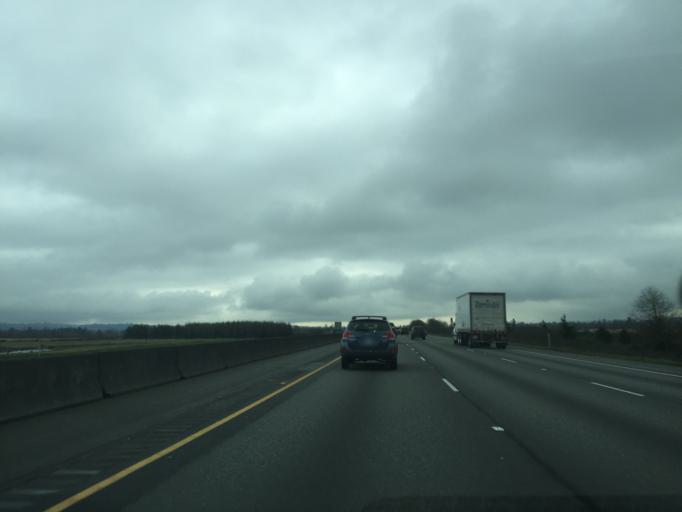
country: US
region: Washington
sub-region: Snohomish County
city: Marysville
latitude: 48.0295
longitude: -122.1769
